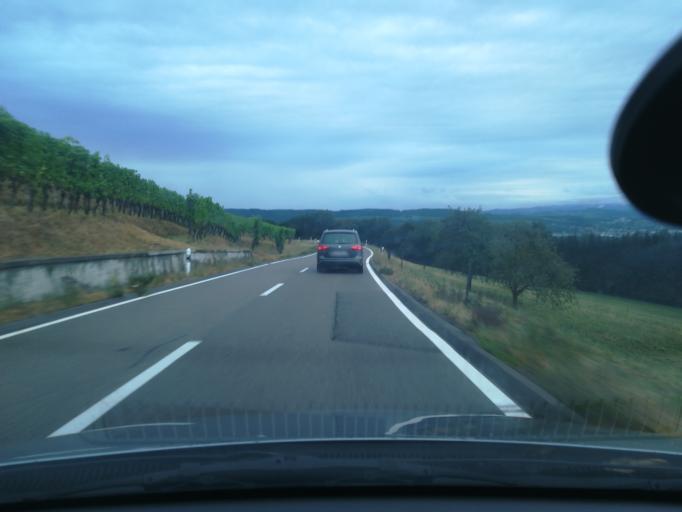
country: CH
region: Thurgau
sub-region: Frauenfeld District
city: Huttwilen
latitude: 47.6089
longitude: 8.8928
